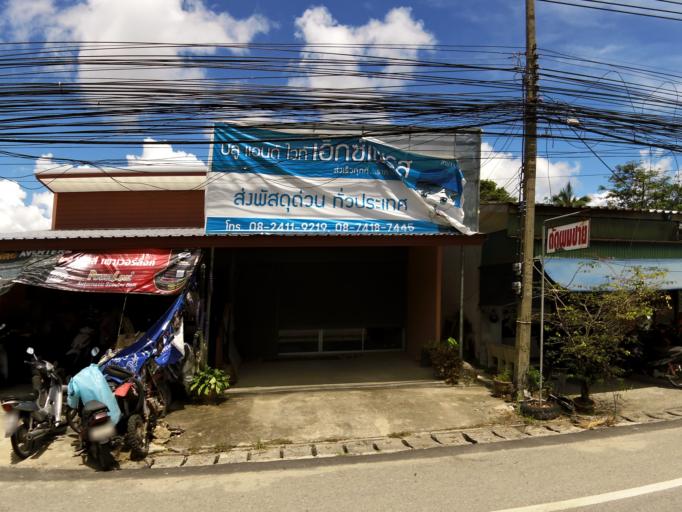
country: TH
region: Phuket
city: Ban Chalong
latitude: 7.8348
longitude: 98.3378
